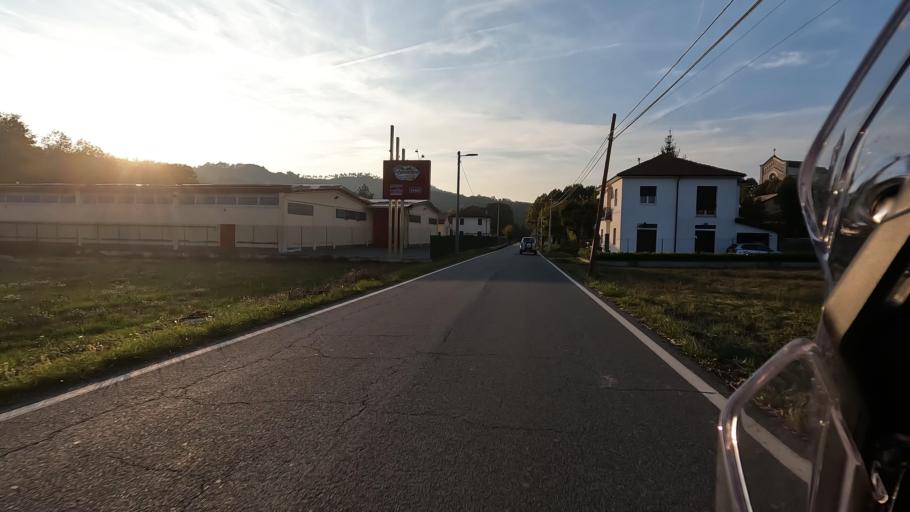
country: IT
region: Liguria
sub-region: Provincia di Savona
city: Sassello
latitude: 44.4998
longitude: 8.4895
